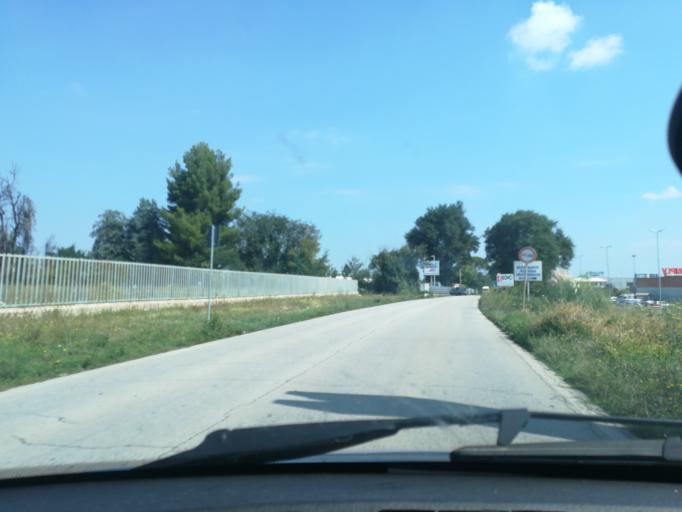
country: IT
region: The Marches
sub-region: Provincia di Macerata
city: Tolentino
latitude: 43.2227
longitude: 13.3324
